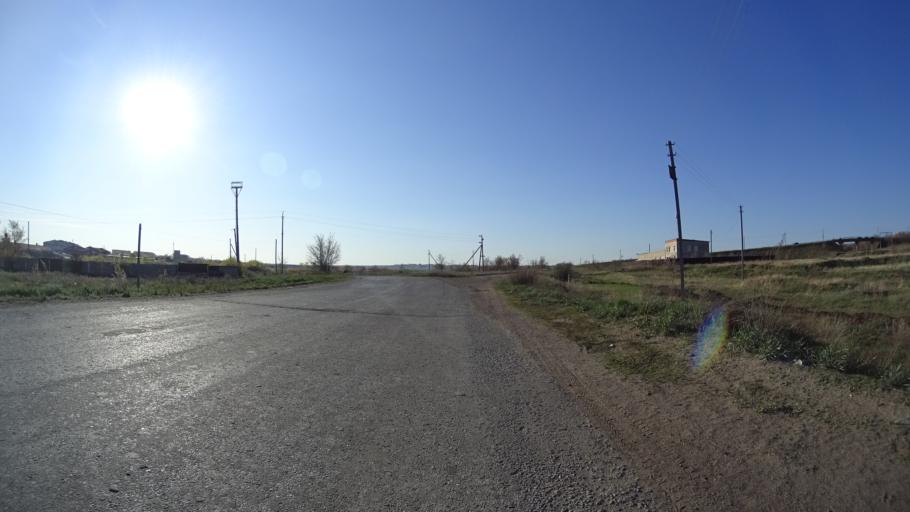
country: RU
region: Chelyabinsk
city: Troitsk
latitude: 54.0775
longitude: 61.6005
